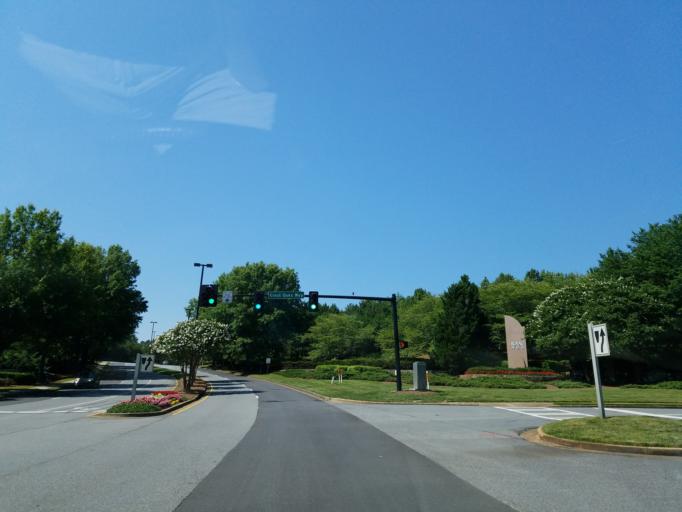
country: US
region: Georgia
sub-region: Fulton County
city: Alpharetta
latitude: 34.0623
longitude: -84.2655
